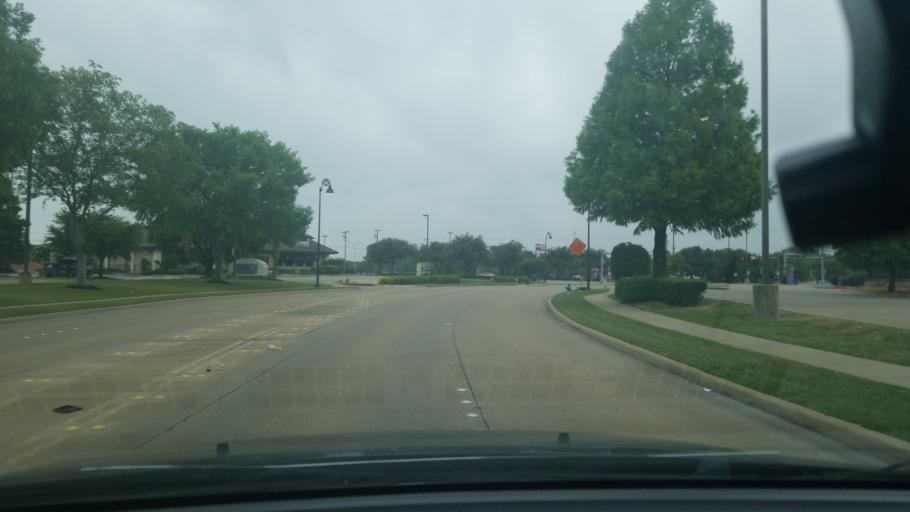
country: US
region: Texas
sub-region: Dallas County
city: Mesquite
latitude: 32.7845
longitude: -96.6259
